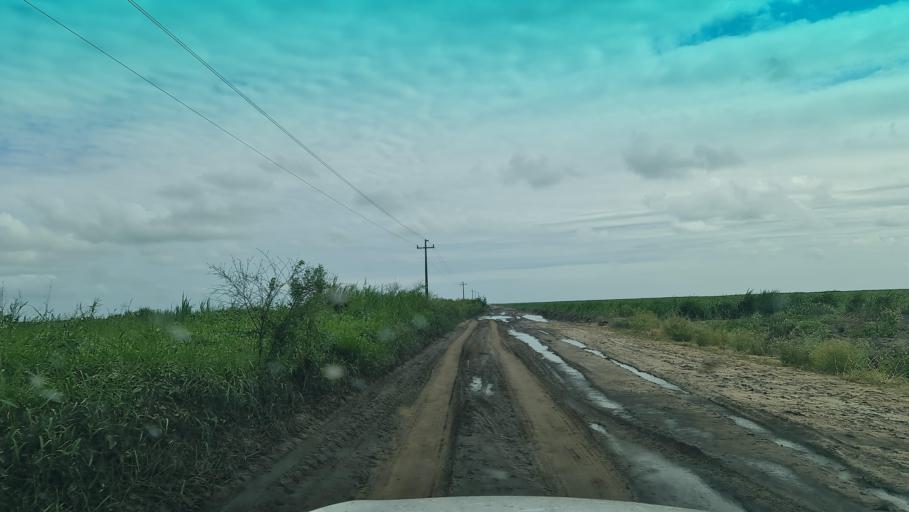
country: MZ
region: Maputo
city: Manhica
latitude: -25.4413
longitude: 32.8403
